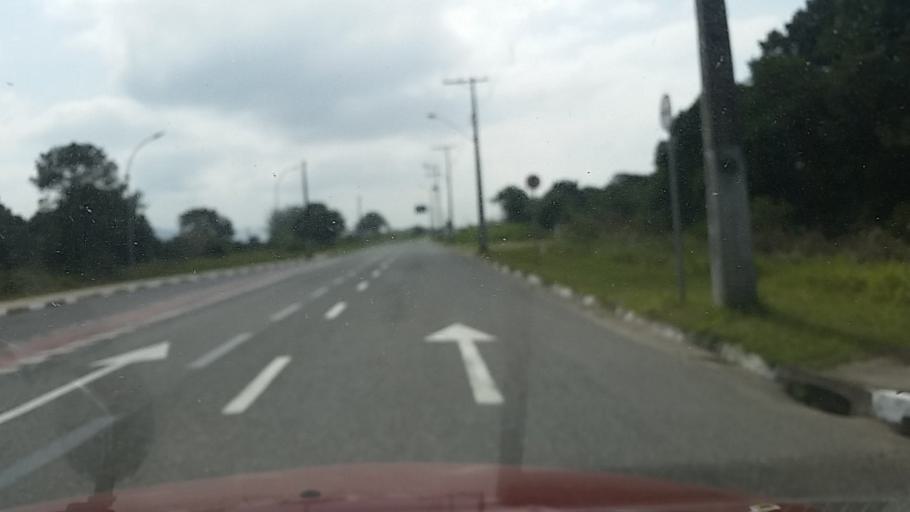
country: BR
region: Sao Paulo
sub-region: Iguape
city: Iguape
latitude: -24.7329
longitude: -47.5415
